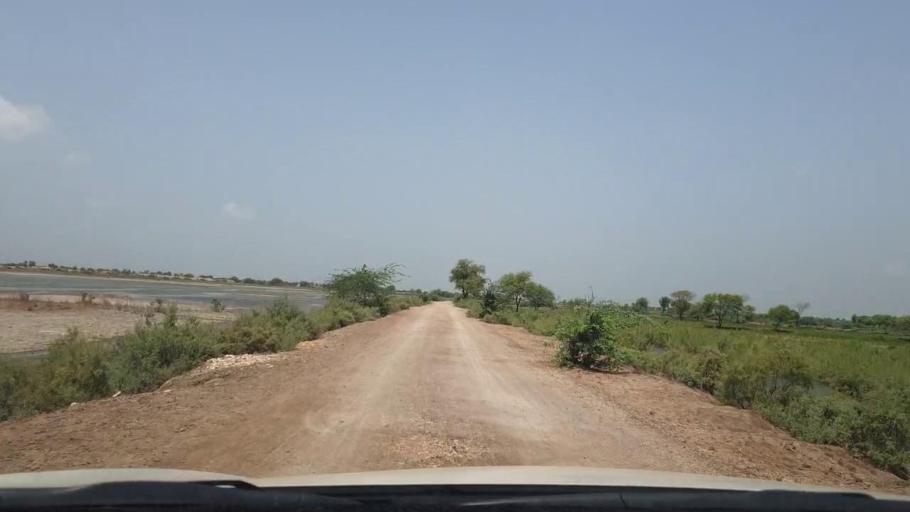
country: PK
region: Sindh
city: Talhar
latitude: 24.9255
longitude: 68.8296
